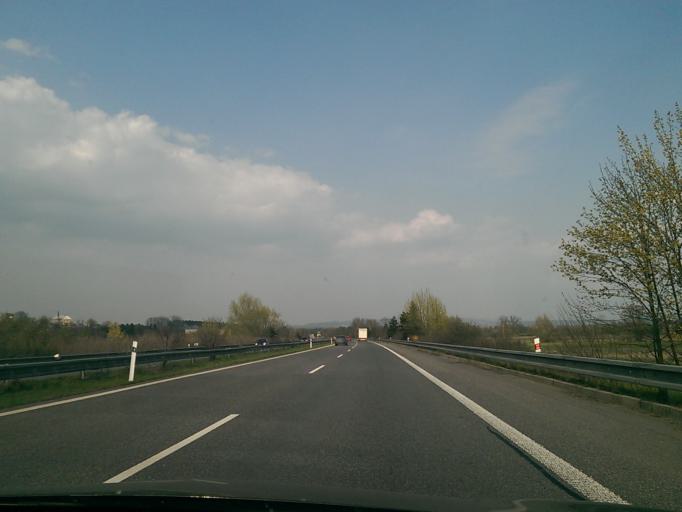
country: CZ
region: Central Bohemia
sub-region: Okres Mlada Boleslav
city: Zd'ar
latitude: 50.5623
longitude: 15.0537
